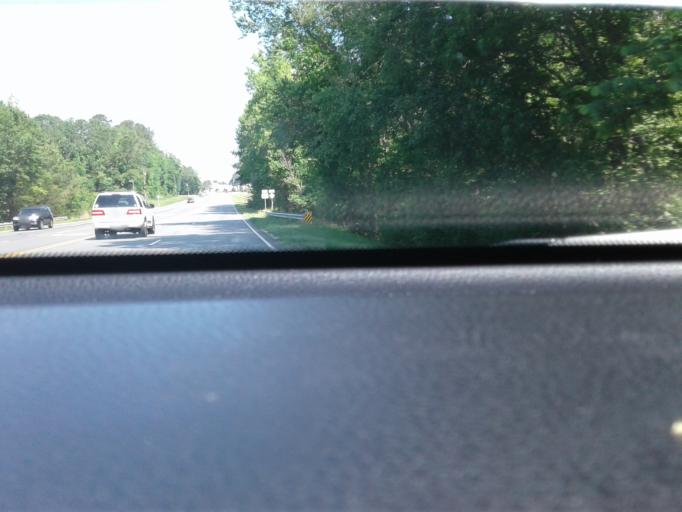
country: US
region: North Carolina
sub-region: Harnett County
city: Buies Creek
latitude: 35.3996
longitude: -78.7343
